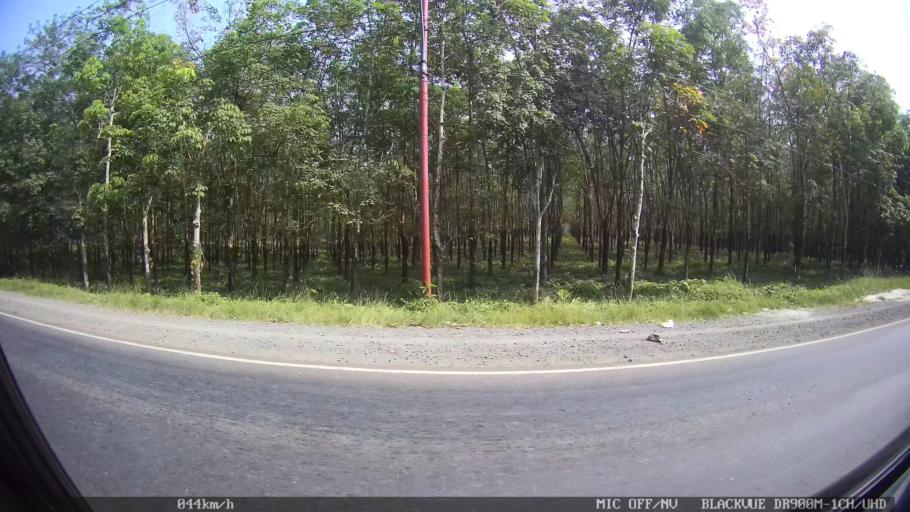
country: ID
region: Lampung
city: Gedongtataan
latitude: -5.3691
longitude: 105.1357
